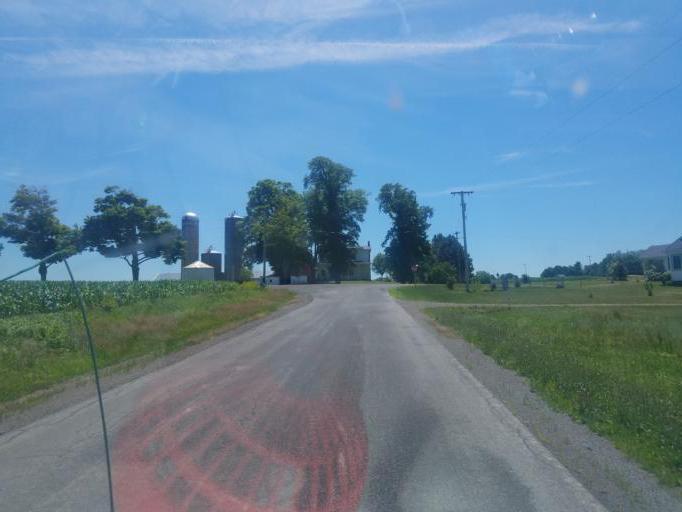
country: US
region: New York
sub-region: Yates County
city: Penn Yan
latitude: 42.6332
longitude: -77.0157
